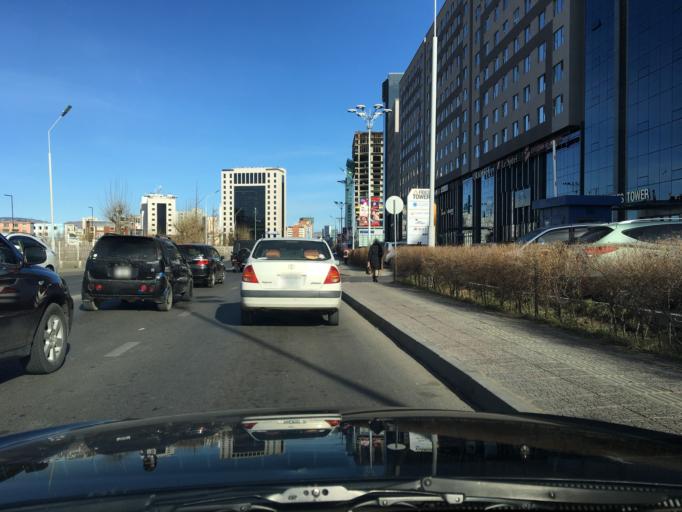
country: MN
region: Ulaanbaatar
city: Ulaanbaatar
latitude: 47.8972
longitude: 106.9084
